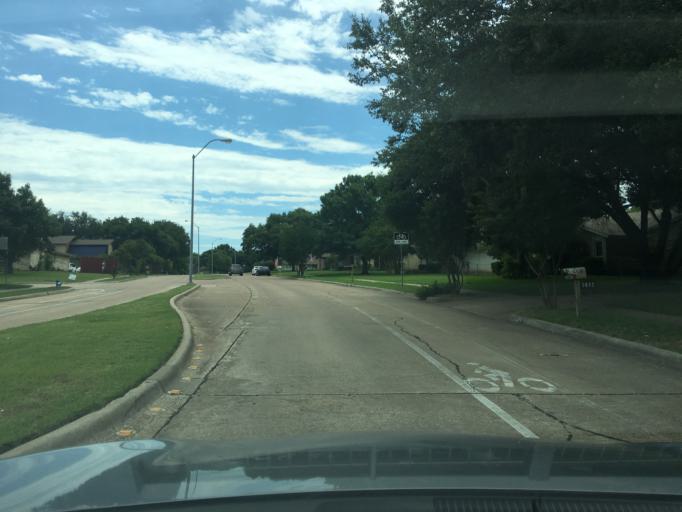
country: US
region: Texas
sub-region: Dallas County
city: Richardson
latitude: 32.9657
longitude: -96.6923
